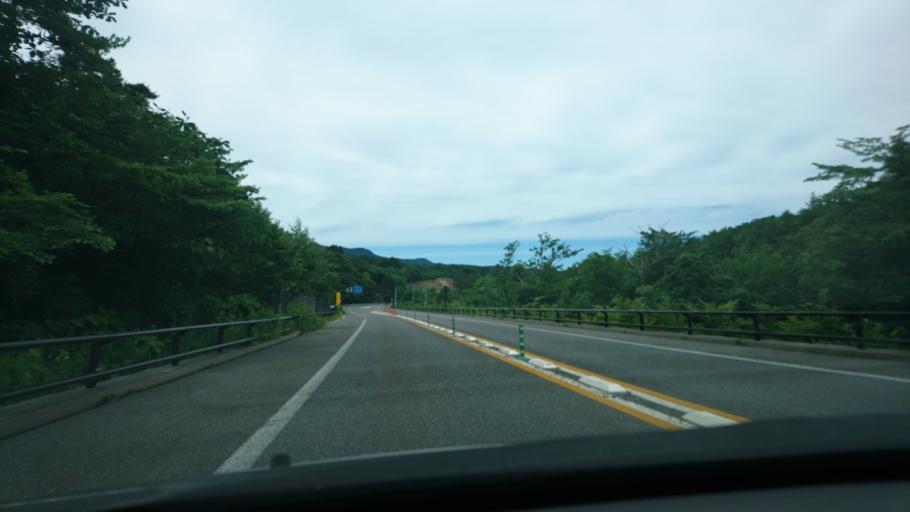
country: JP
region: Iwate
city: Miyako
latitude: 39.9372
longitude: 141.8428
